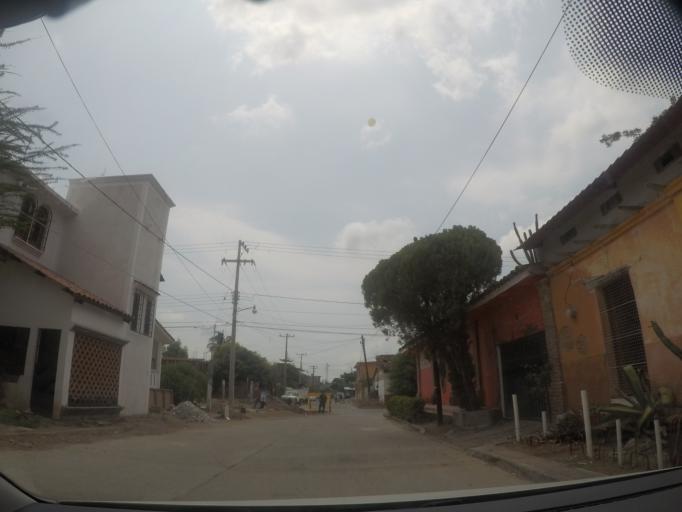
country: MX
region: Oaxaca
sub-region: El Espinal
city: El Espinal
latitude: 16.4885
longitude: -95.0448
